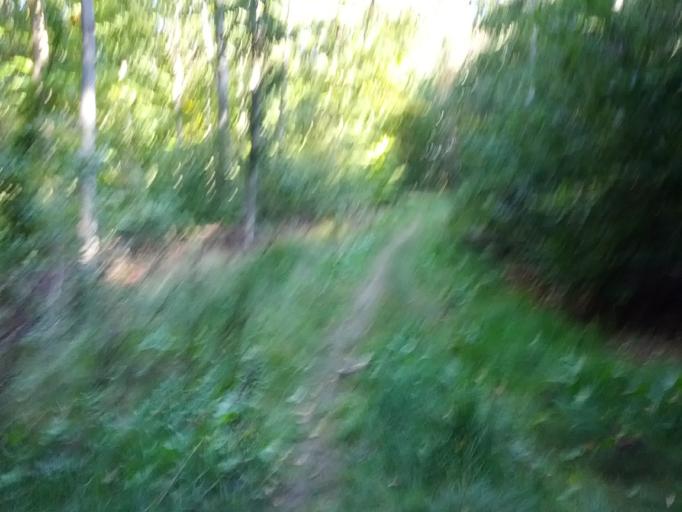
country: DE
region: Thuringia
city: Krauthausen
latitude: 51.0054
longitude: 10.2913
